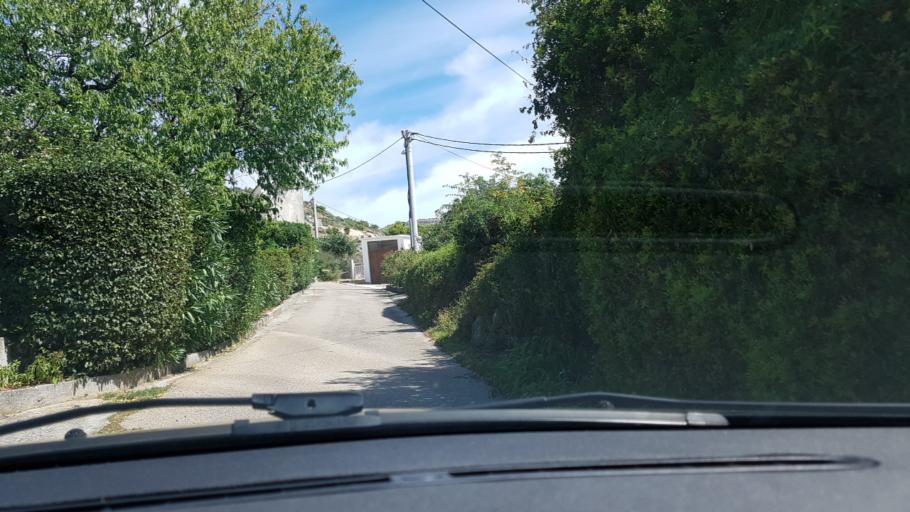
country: HR
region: Splitsko-Dalmatinska
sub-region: Grad Trogir
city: Trogir
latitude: 43.5223
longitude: 16.2272
